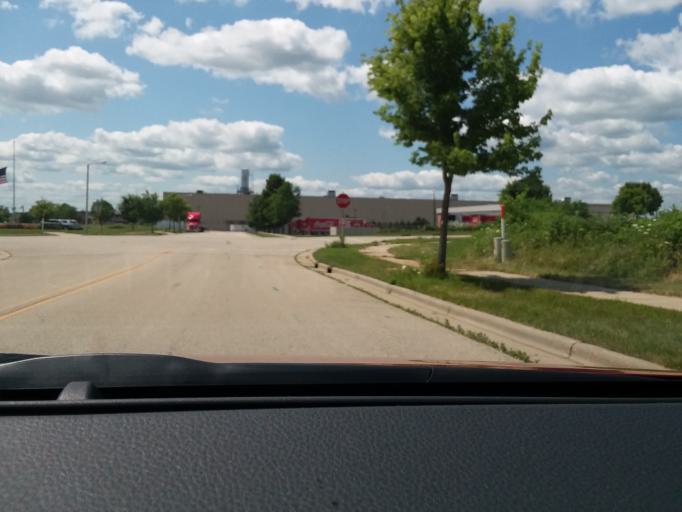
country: US
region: Wisconsin
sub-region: Dane County
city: Windsor
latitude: 43.1962
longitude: -89.3301
